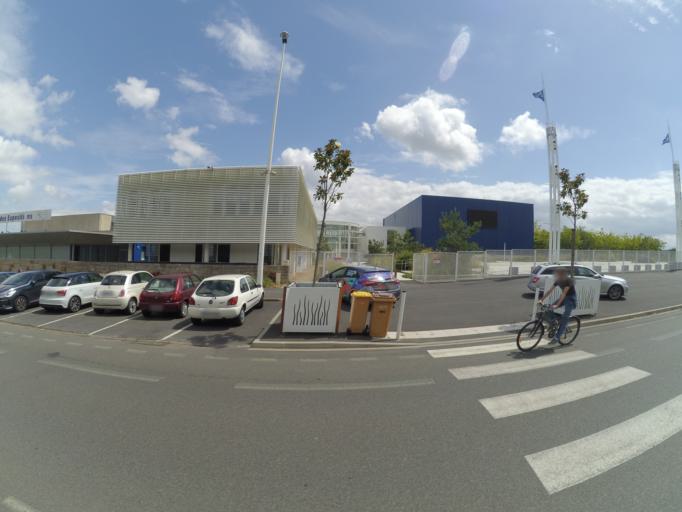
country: FR
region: Brittany
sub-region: Departement des Cotes-d'Armor
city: Saint-Brieuc
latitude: 48.4992
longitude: -2.7647
